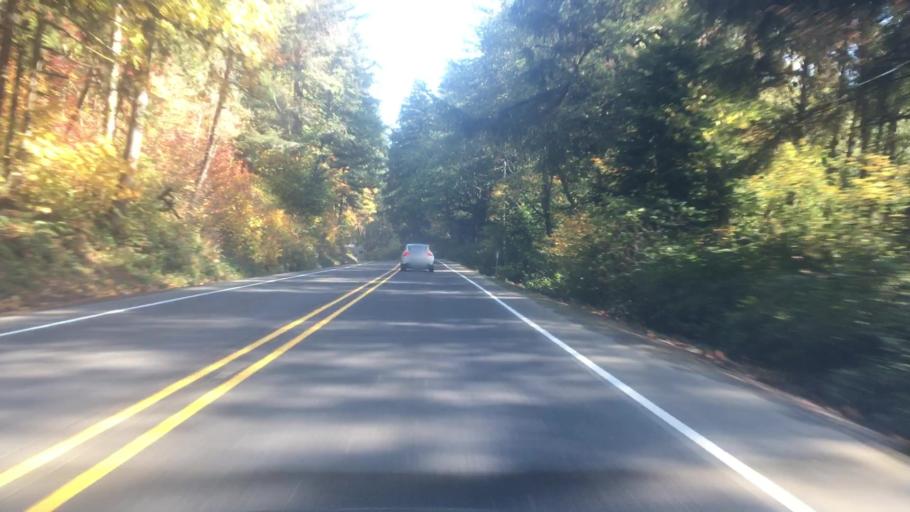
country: US
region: Oregon
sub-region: Lincoln County
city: Rose Lodge
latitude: 45.0554
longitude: -123.7603
